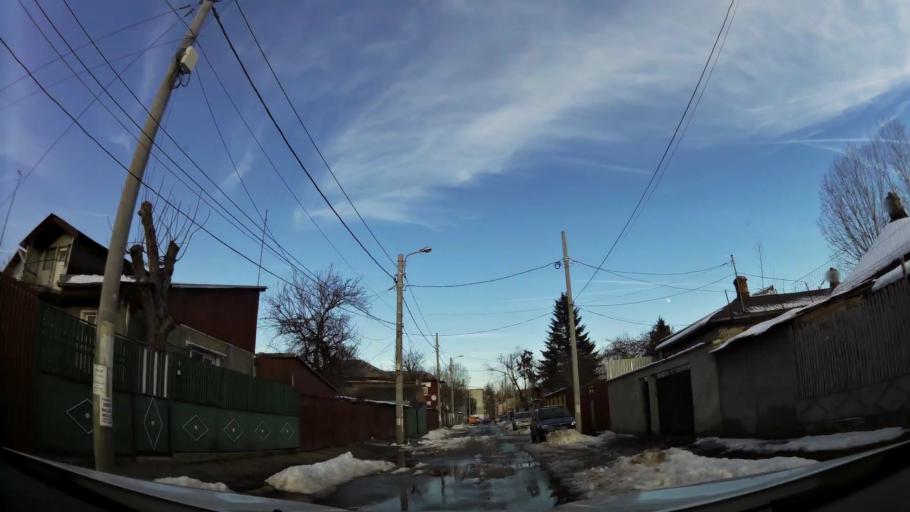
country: RO
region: Bucuresti
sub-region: Municipiul Bucuresti
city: Bucuresti
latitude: 44.3881
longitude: 26.0814
